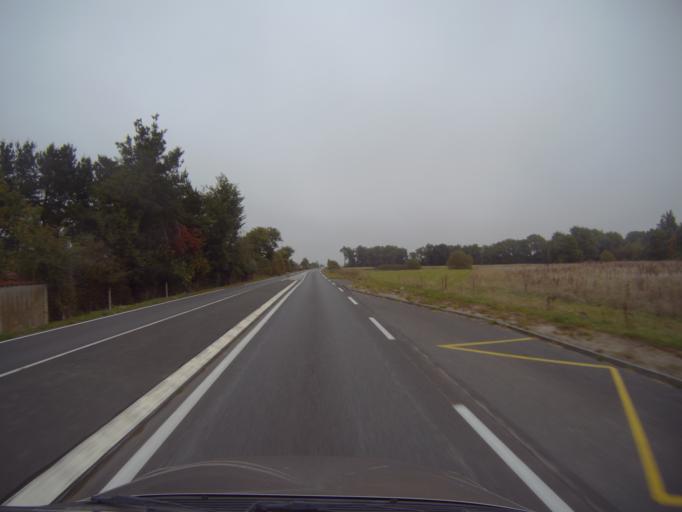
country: FR
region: Pays de la Loire
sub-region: Departement de la Vendee
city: La Bernardiere
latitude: 47.0287
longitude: -1.2640
